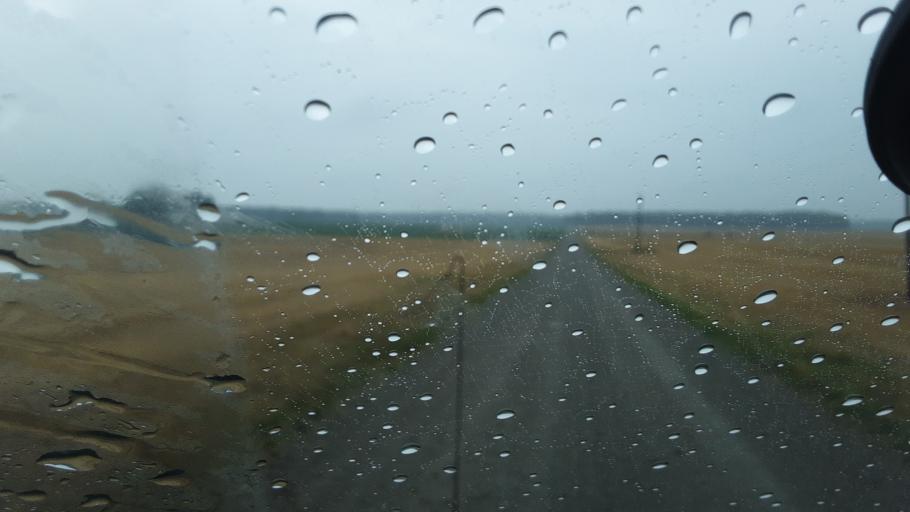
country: US
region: Indiana
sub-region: DeKalb County
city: Butler
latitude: 41.4139
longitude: -84.8129
